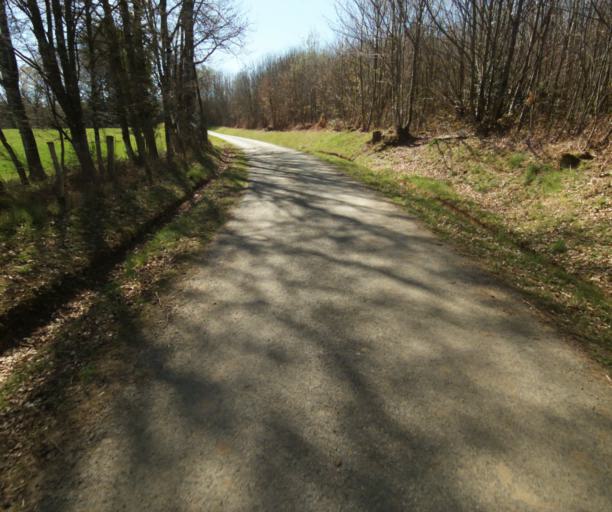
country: FR
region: Limousin
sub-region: Departement de la Correze
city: Uzerche
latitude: 45.3945
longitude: 1.6084
